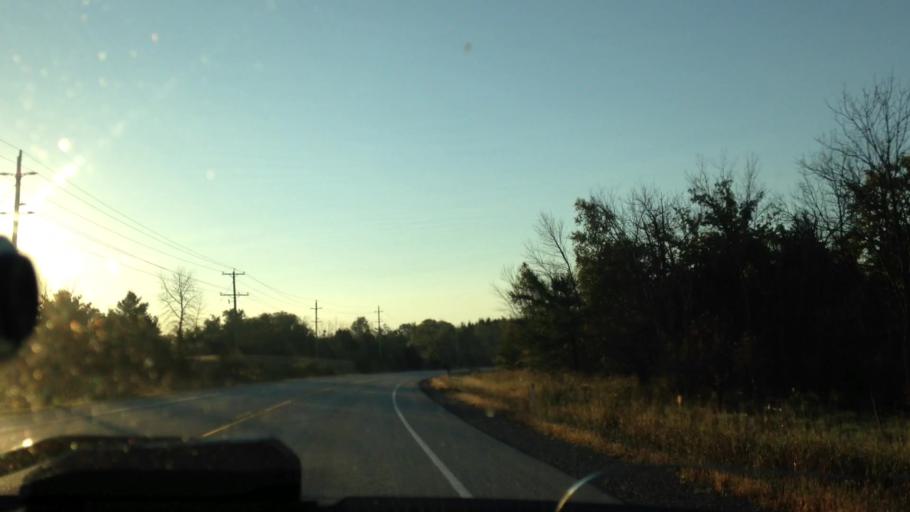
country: US
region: Wisconsin
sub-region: Washington County
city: Newburg
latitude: 43.4064
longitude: -87.9939
